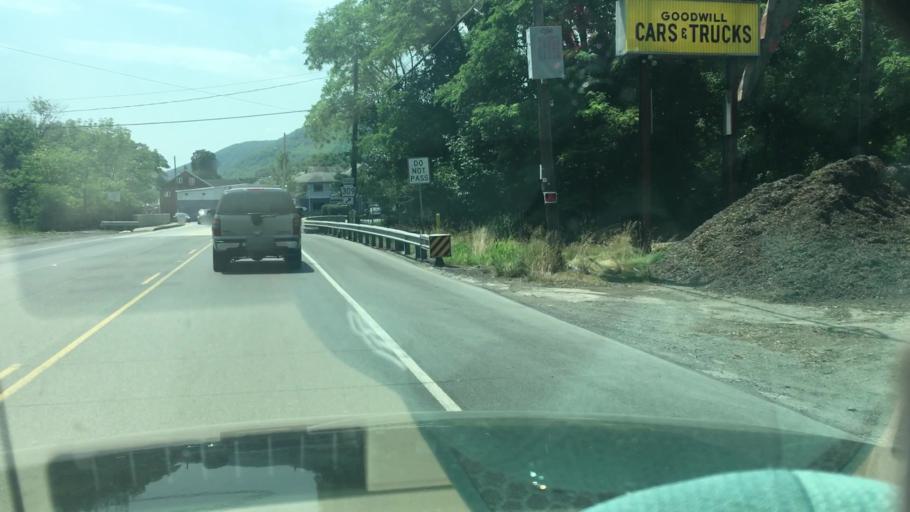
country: US
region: Pennsylvania
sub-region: Schuylkill County
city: Tamaqua
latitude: 40.8060
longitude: -75.9715
